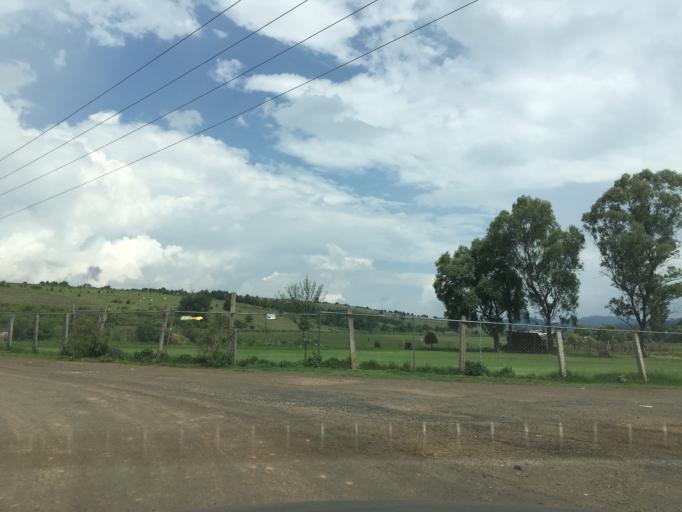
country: MX
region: Michoacan
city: Acuitzio del Canje
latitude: 19.5224
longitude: -101.2555
